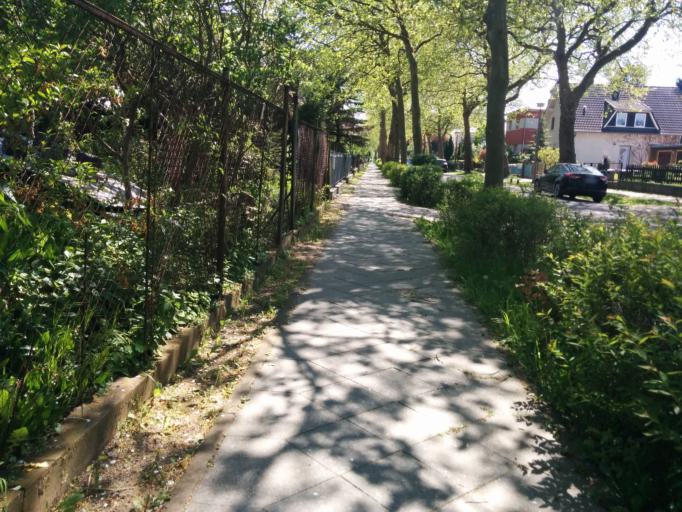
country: DE
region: Berlin
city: Biesdorf
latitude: 52.5219
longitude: 13.5544
